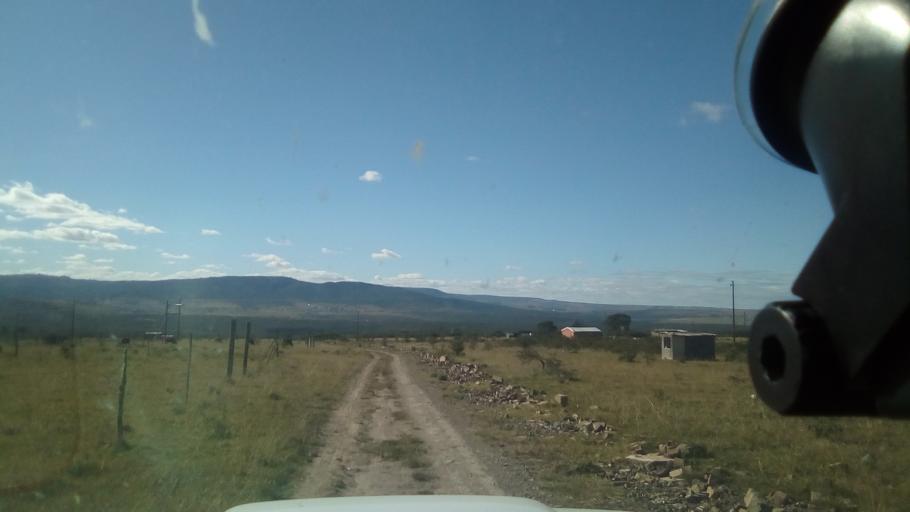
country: ZA
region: Eastern Cape
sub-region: Buffalo City Metropolitan Municipality
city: Bhisho
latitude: -32.7802
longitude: 27.3349
